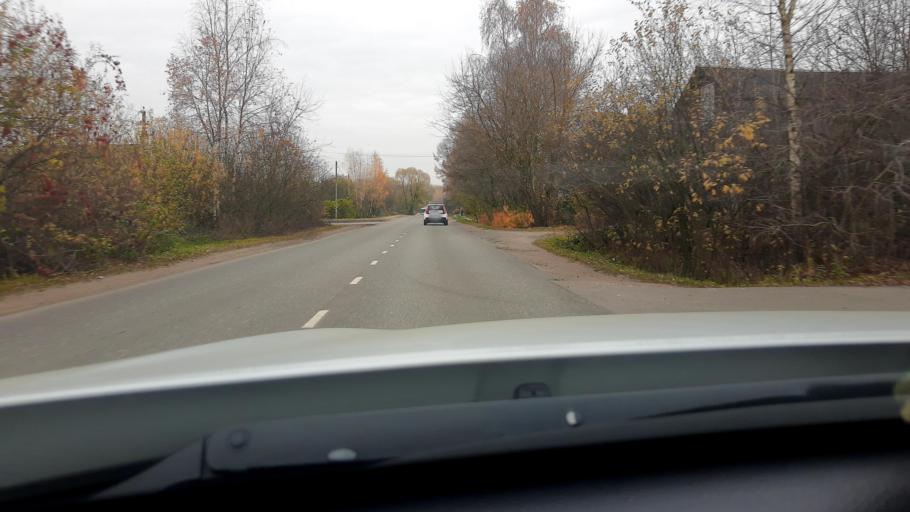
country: RU
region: Moskovskaya
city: Dolgoprudnyy
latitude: 55.9341
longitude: 37.4794
